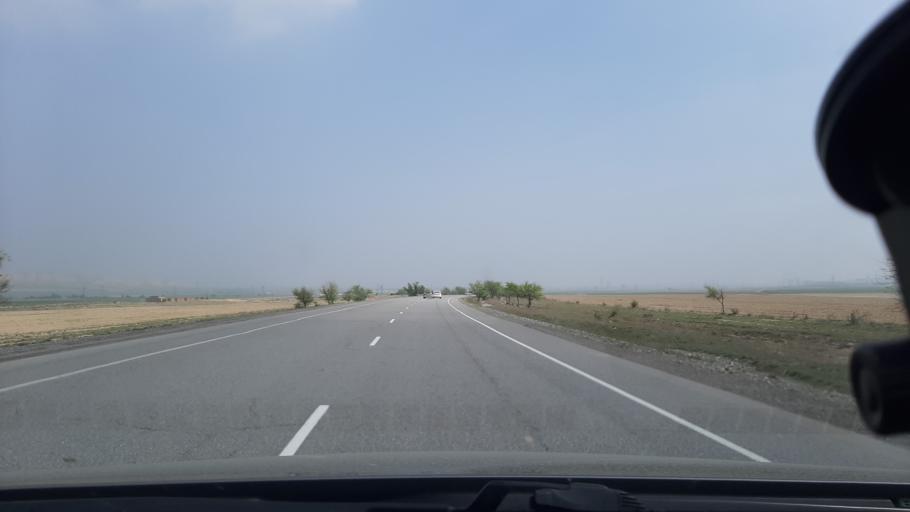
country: UZ
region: Toshkent
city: Bekobod
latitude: 40.1154
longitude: 69.1995
